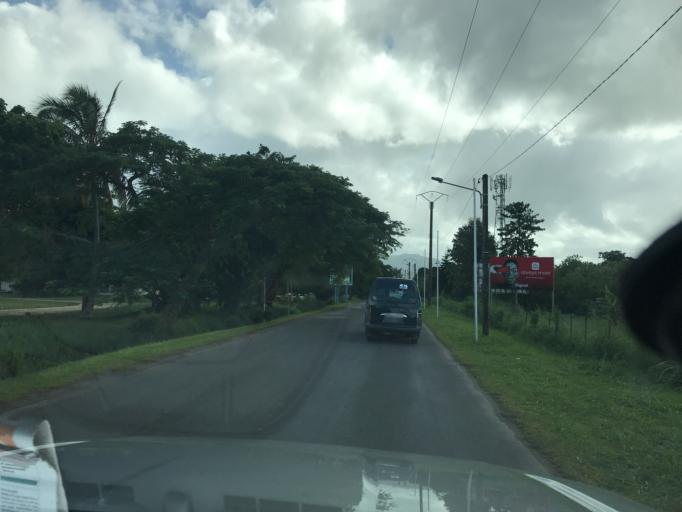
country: VU
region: Shefa
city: Port-Vila
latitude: -17.7041
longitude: 168.3183
